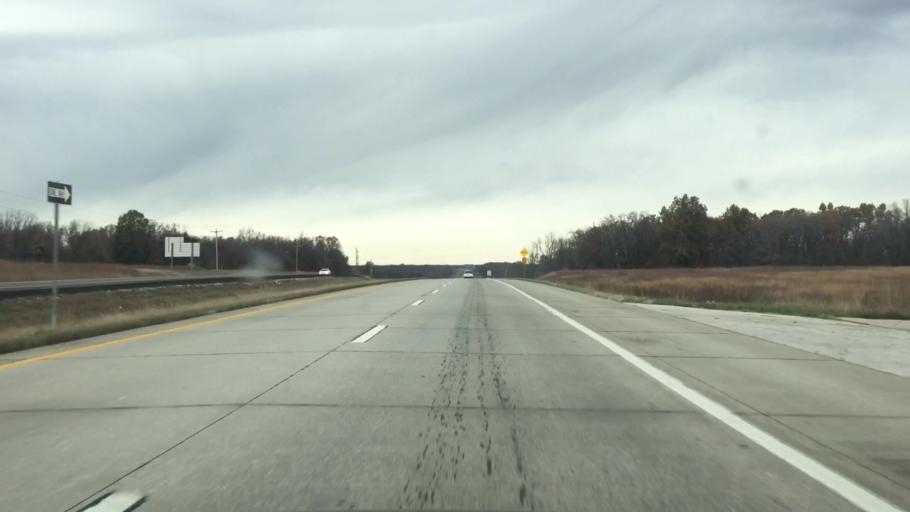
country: US
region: Missouri
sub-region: Saint Clair County
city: Osceola
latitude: 38.0459
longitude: -93.6843
